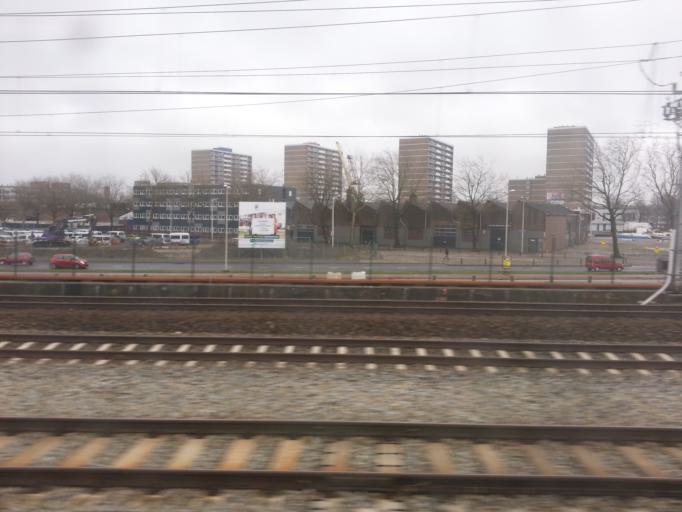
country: NL
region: South Holland
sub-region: Gemeente Den Haag
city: The Hague
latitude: 52.0603
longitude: 4.3101
